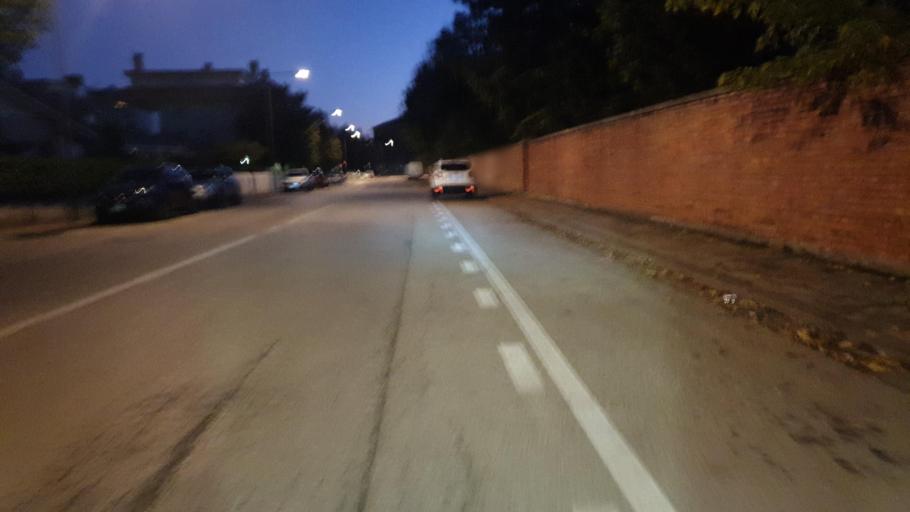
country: IT
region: Veneto
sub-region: Provincia di Padova
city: Oltre Brenta
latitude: 45.4131
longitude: 12.0054
